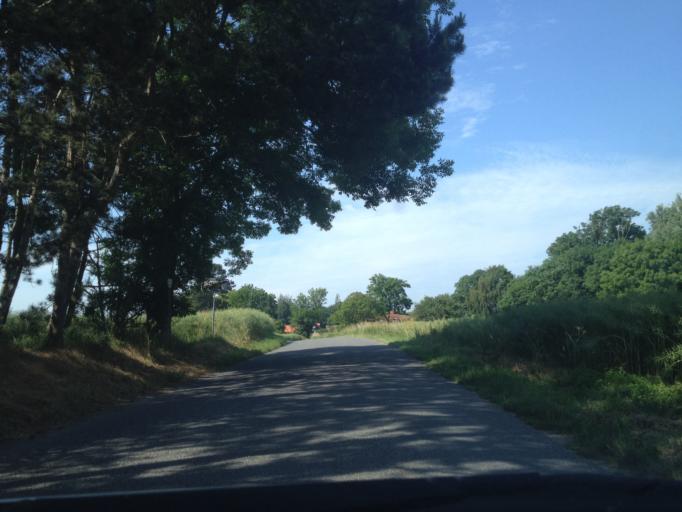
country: DK
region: Central Jutland
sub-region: Samso Kommune
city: Tranebjerg
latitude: 55.8141
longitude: 10.5548
